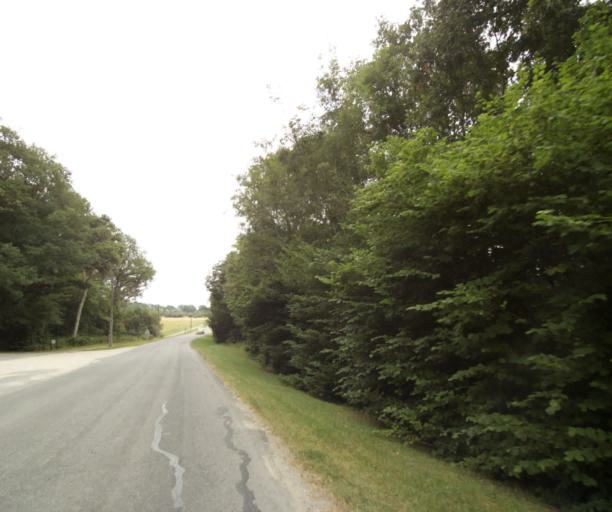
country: FR
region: Centre
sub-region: Departement du Loiret
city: Marigny-les-Usages
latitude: 47.9605
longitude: 2.0017
